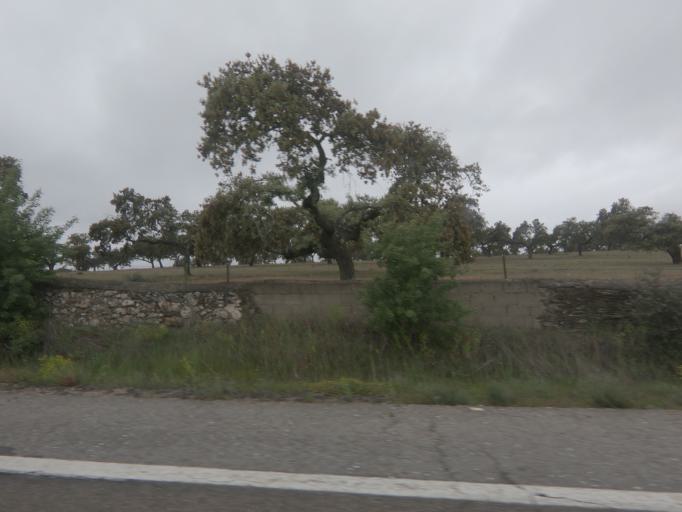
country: ES
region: Extremadura
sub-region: Provincia de Badajoz
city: Puebla de Obando
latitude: 39.2270
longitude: -6.5721
